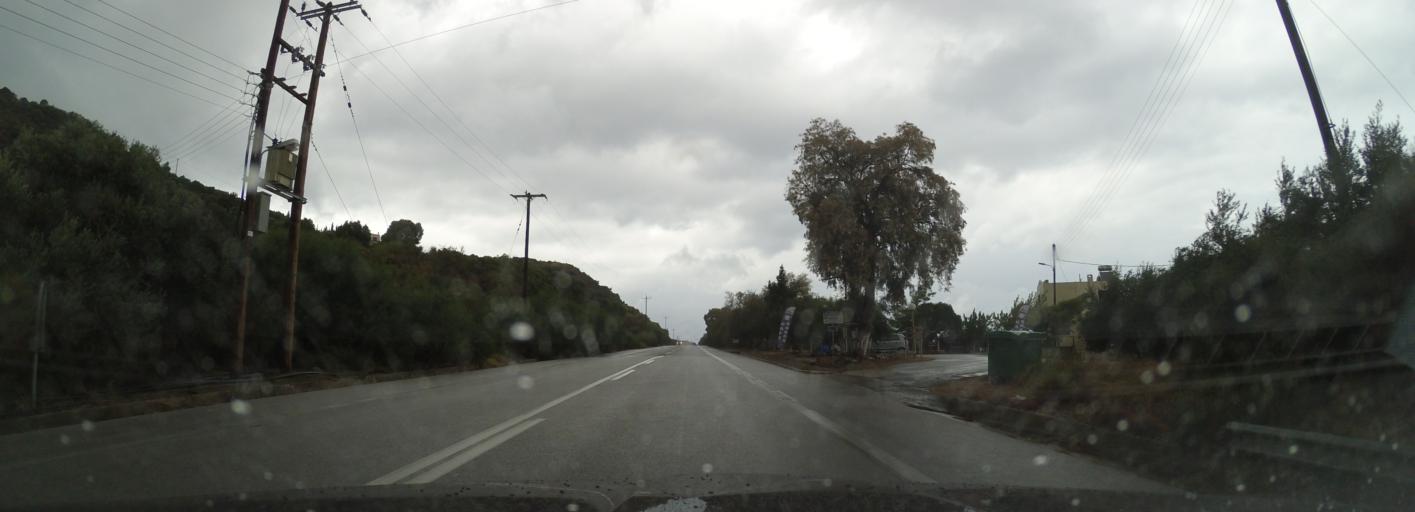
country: GR
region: Crete
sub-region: Nomos Irakleiou
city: Gazi
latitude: 35.4027
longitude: 24.9956
